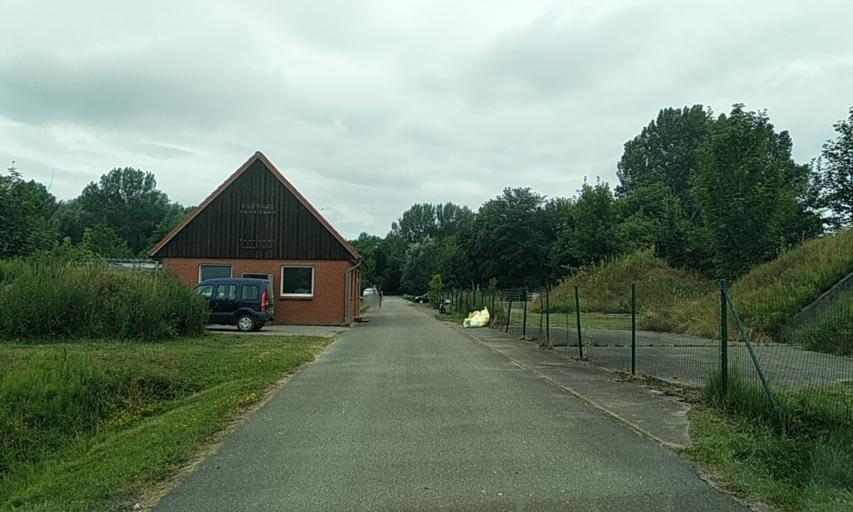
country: DE
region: Schleswig-Holstein
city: Brodersby
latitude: 54.6452
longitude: 10.0102
